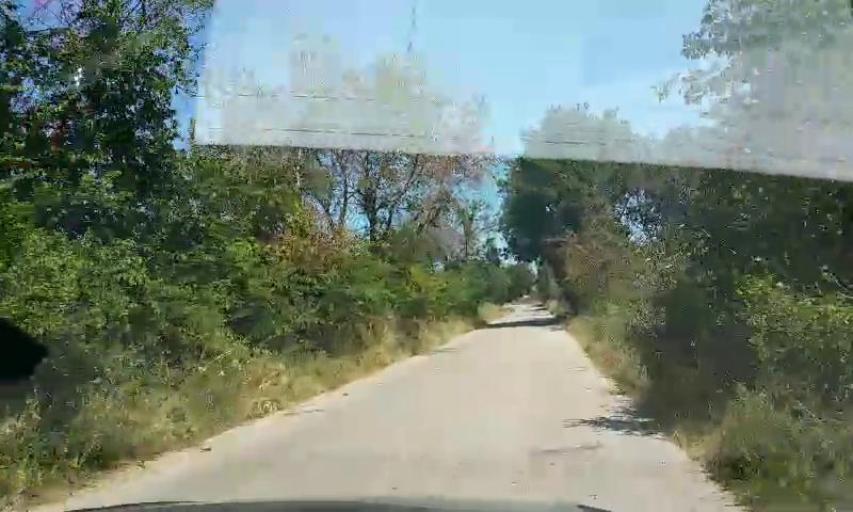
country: IT
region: Molise
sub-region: Provincia di Campobasso
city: Guglionesi
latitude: 41.9526
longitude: 14.9010
